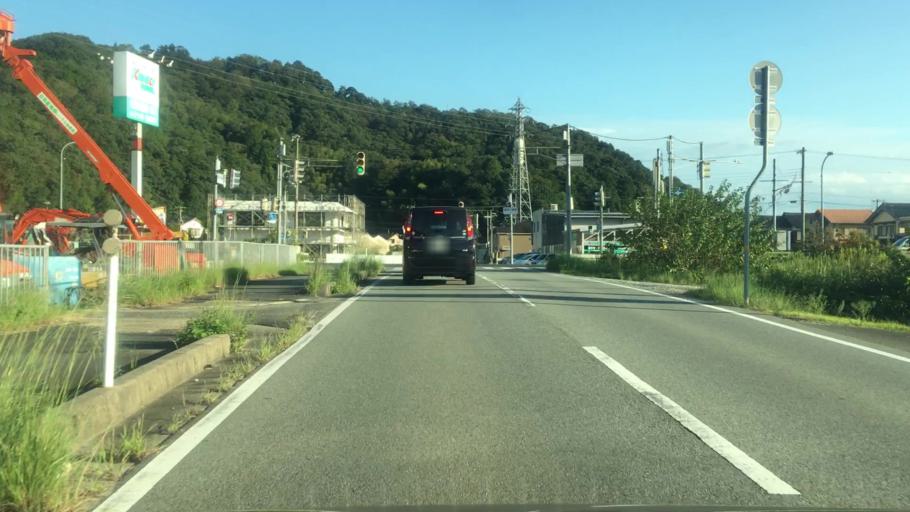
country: JP
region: Hyogo
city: Toyooka
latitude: 35.5593
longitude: 134.8244
